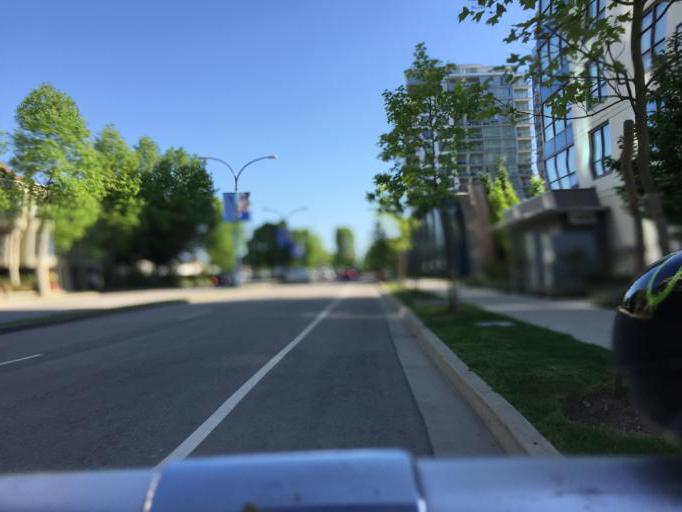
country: CA
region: British Columbia
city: Richmond
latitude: 49.1687
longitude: -123.1403
